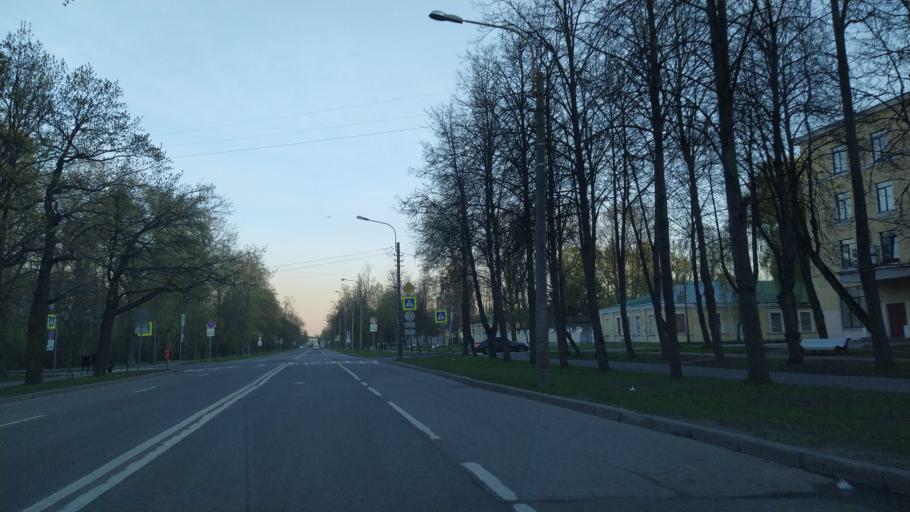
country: RU
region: St.-Petersburg
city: Pushkin
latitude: 59.7087
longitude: 30.4034
